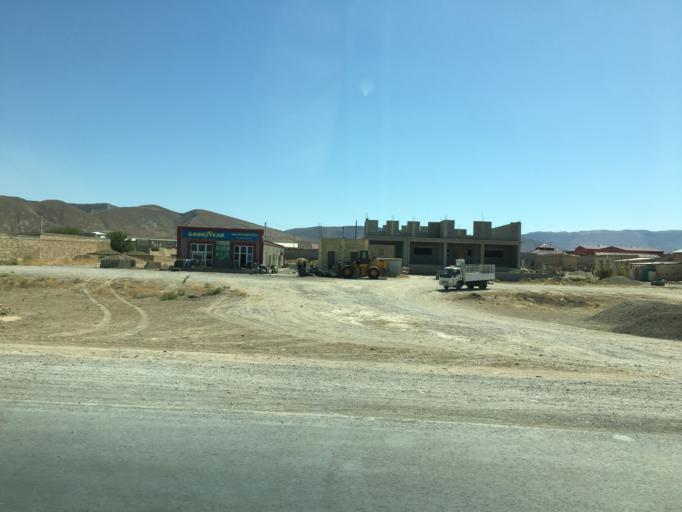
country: TM
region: Balkan
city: Serdar
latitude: 38.9771
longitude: 56.3098
